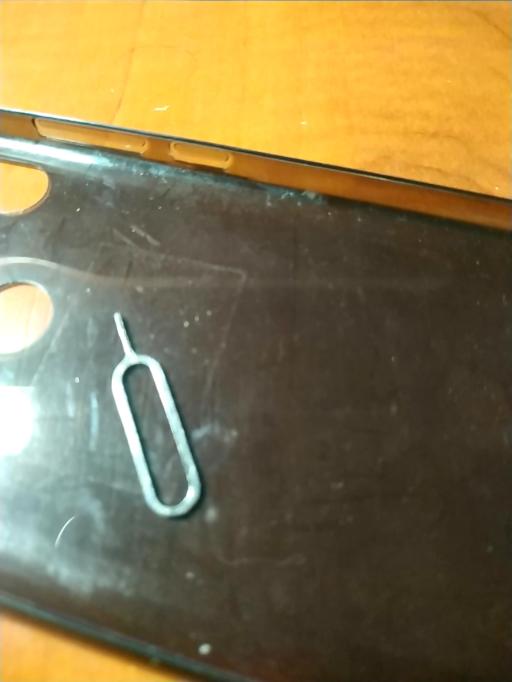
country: RU
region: Kaluga
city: Iznoski
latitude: 54.8598
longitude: 35.3399
